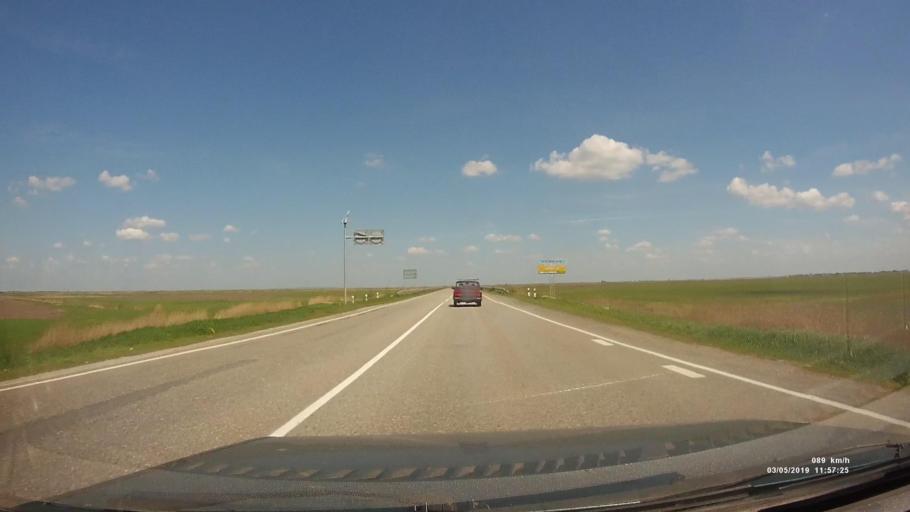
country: RU
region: Rostov
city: Bagayevskaya
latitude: 47.2063
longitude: 40.3095
